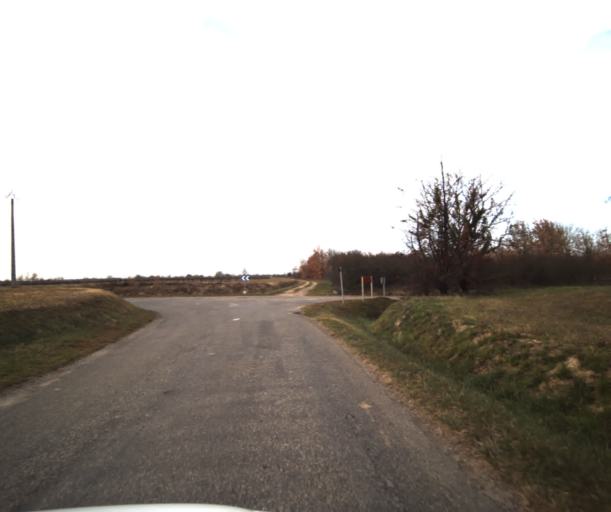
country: FR
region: Midi-Pyrenees
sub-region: Departement du Tarn-et-Garonne
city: Campsas
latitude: 43.8989
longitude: 1.3420
